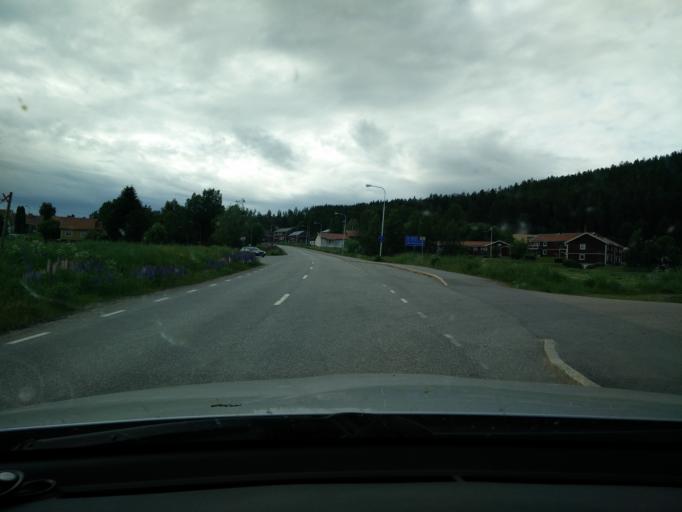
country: SE
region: Gaevleborg
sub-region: Hudiksvalls Kommun
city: Delsbo
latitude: 62.1075
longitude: 16.7160
